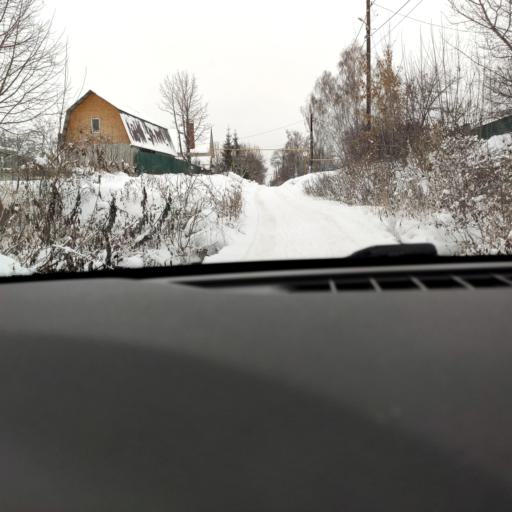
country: RU
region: Samara
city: Smyshlyayevka
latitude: 53.2433
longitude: 50.3468
